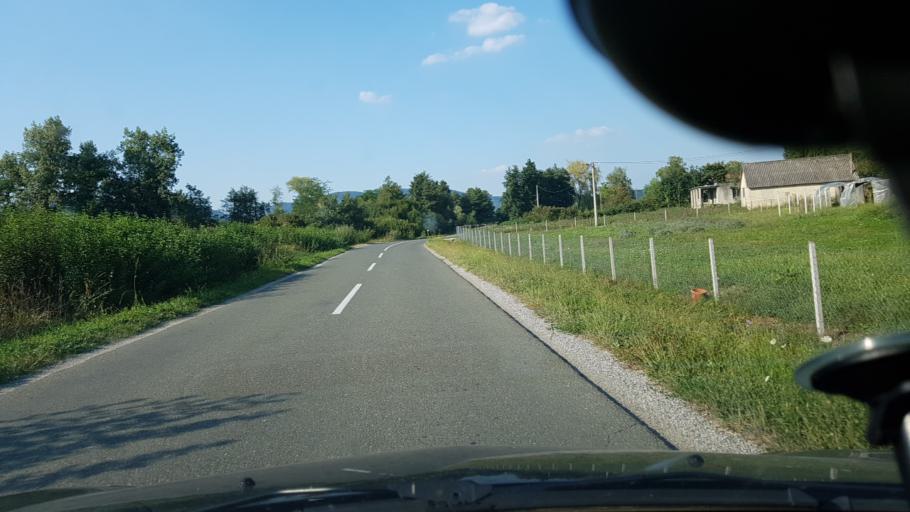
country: SI
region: Bistrica ob Sotli
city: Bistrica ob Sotli
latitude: 46.0075
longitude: 15.7140
